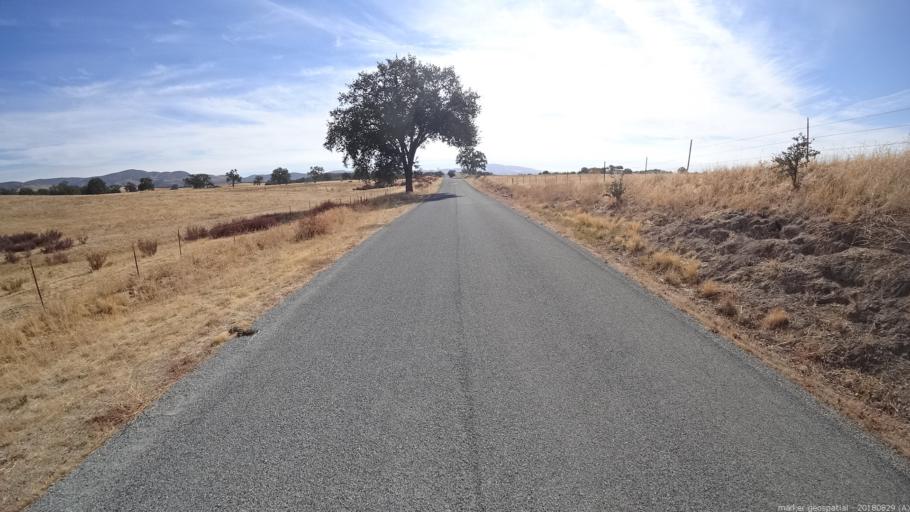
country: US
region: California
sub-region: Monterey County
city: King City
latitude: 35.9663
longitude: -121.1387
